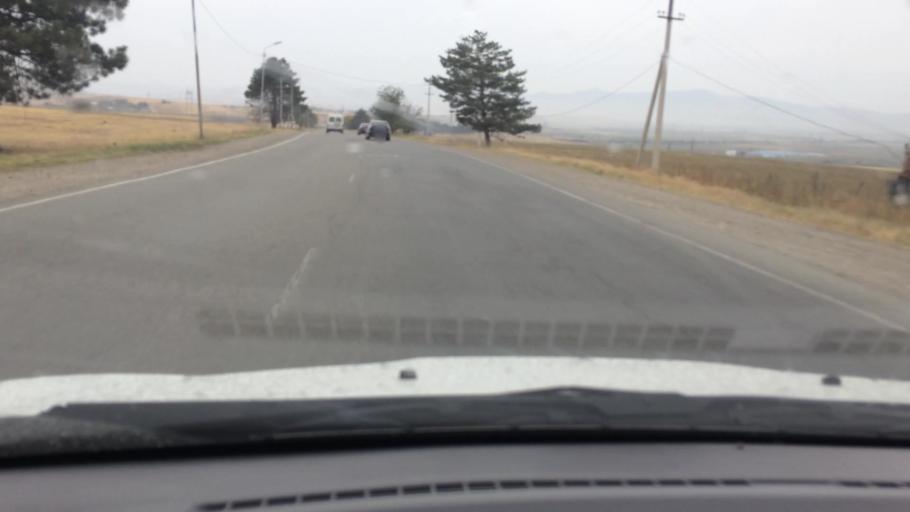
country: GE
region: Kvemo Kartli
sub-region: Marneuli
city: Marneuli
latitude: 41.5132
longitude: 44.7891
